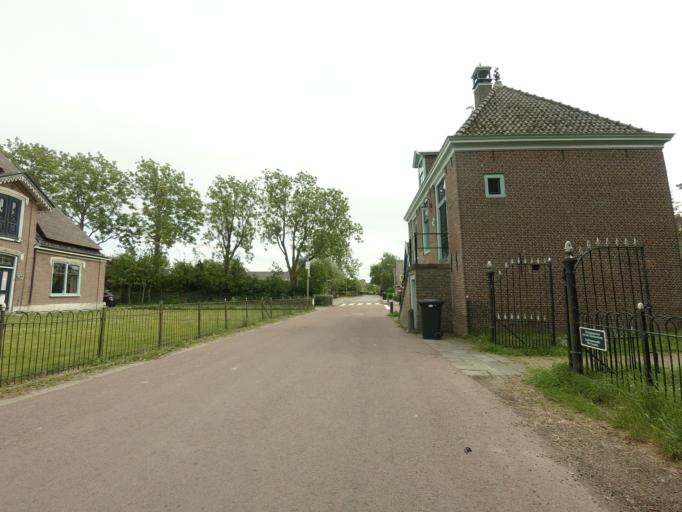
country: NL
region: North Holland
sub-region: Gemeente Hoorn
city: Hoorn
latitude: 52.6346
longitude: 5.1221
